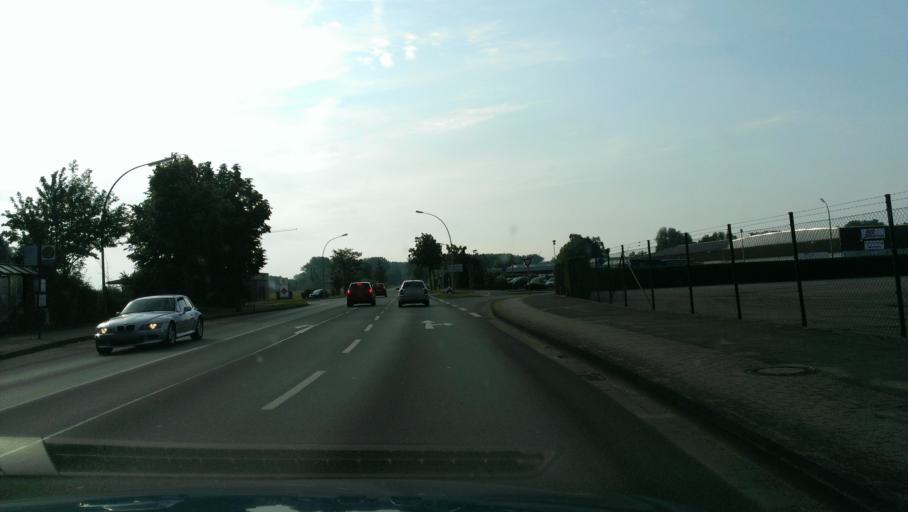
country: DE
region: North Rhine-Westphalia
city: Sendenhorst
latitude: 51.8413
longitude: 7.8424
